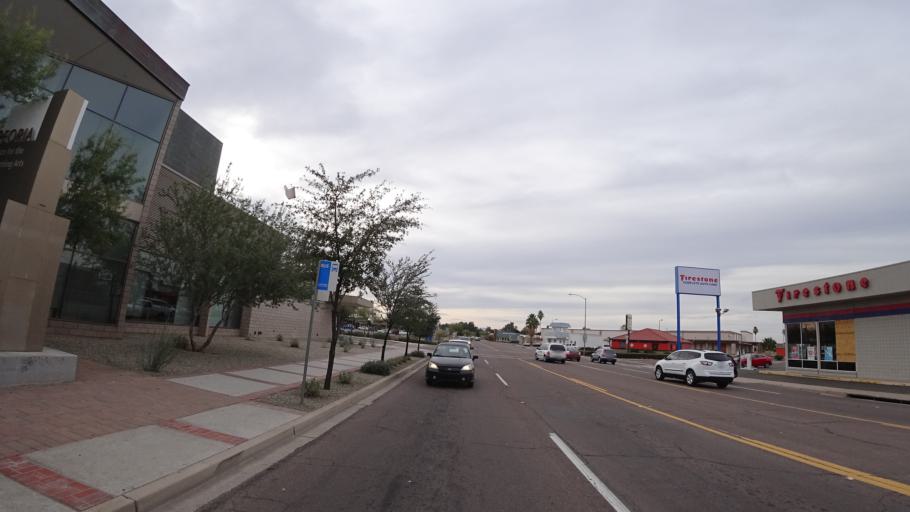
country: US
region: Arizona
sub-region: Maricopa County
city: Peoria
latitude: 33.5816
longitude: -112.2392
